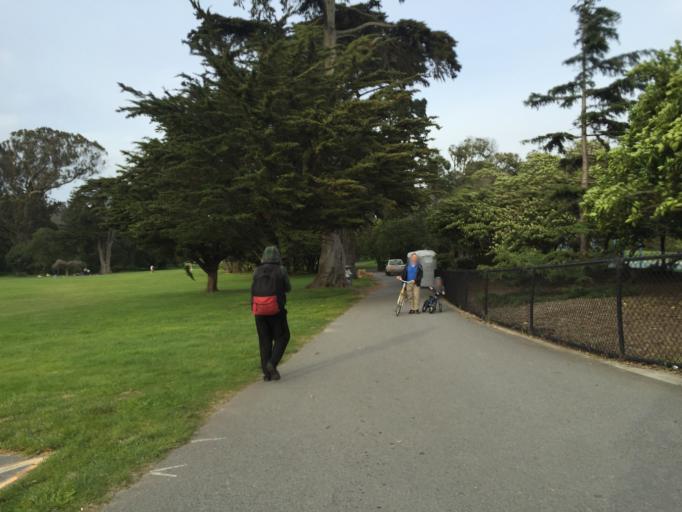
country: US
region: California
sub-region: San Francisco County
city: San Francisco
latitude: 37.7685
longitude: -122.4581
